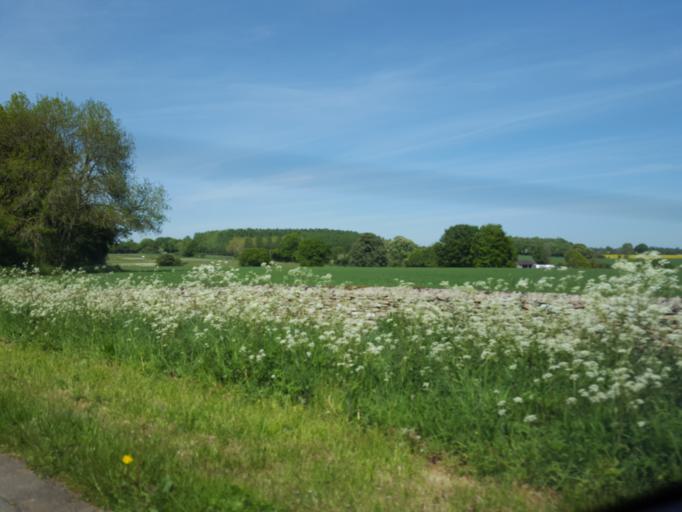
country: GB
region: England
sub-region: Gloucestershire
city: Coates
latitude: 51.6951
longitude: -2.0183
